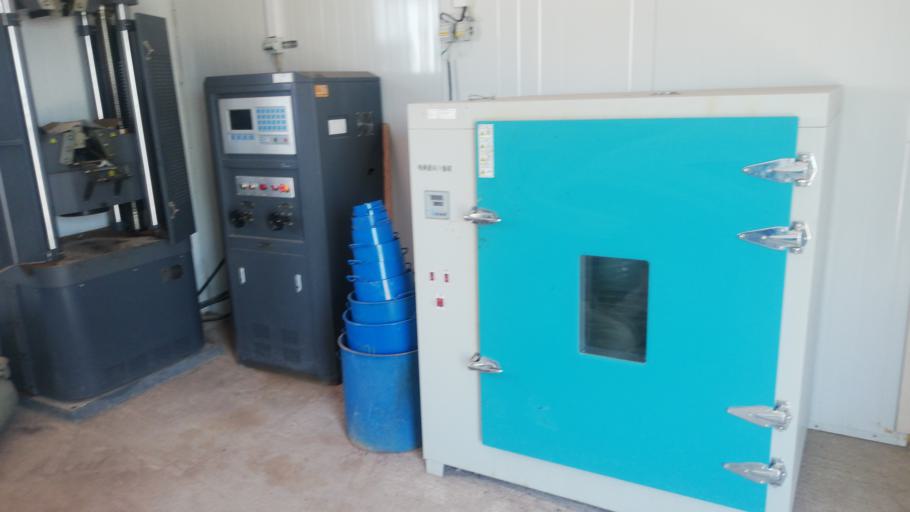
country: KZ
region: Qaraghandy
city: Balqash
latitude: 46.6461
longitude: 74.3968
